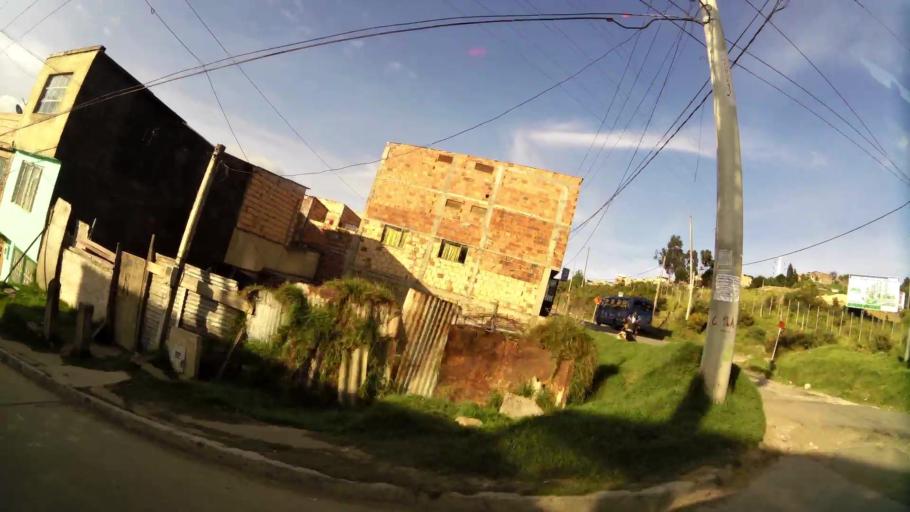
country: CO
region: Bogota D.C.
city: Bogota
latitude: 4.5421
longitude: -74.0967
